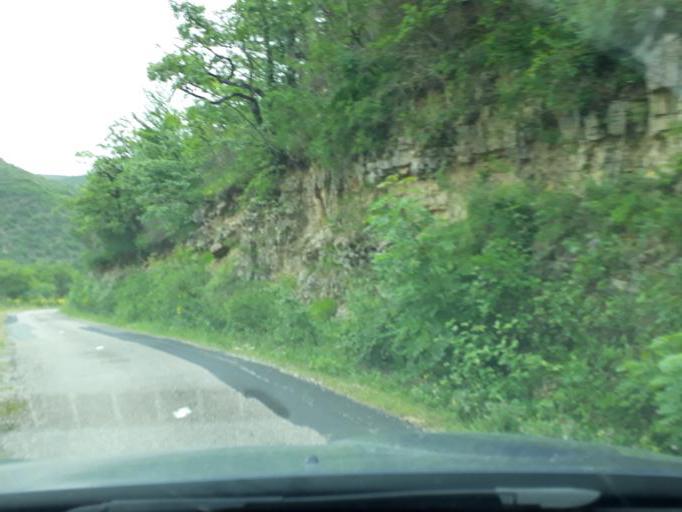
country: FR
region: Languedoc-Roussillon
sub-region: Departement de l'Herault
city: Lodeve
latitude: 43.7965
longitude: 3.2692
